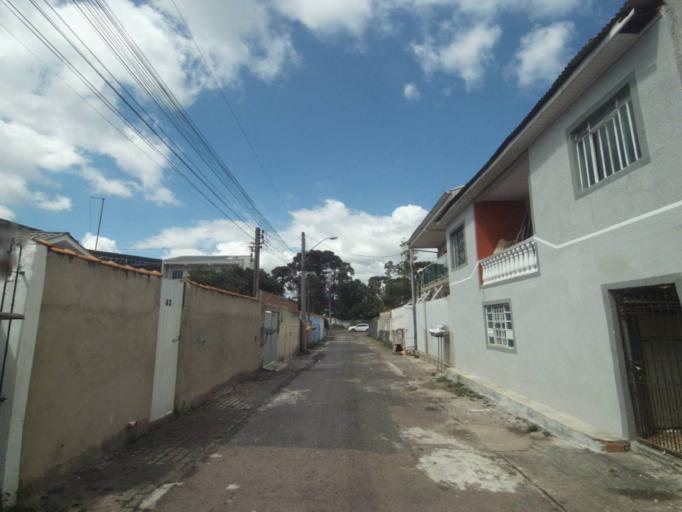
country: BR
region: Parana
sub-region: Curitiba
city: Curitiba
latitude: -25.5099
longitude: -49.3278
